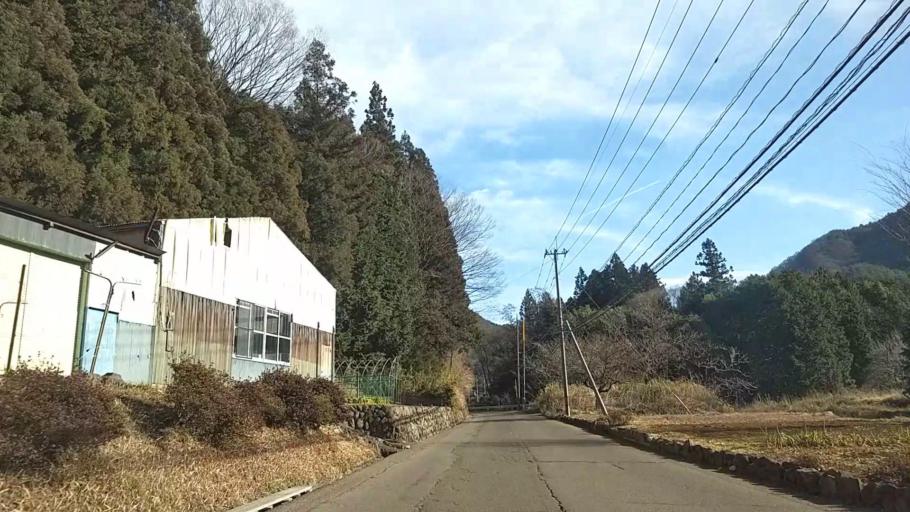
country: JP
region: Yamanashi
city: Otsuki
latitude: 35.5327
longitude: 138.9129
